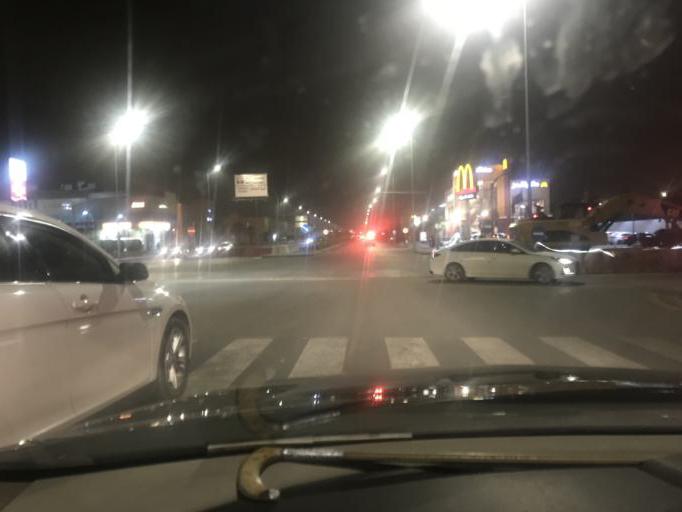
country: SA
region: Ar Riyad
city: Riyadh
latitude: 24.7123
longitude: 46.7950
